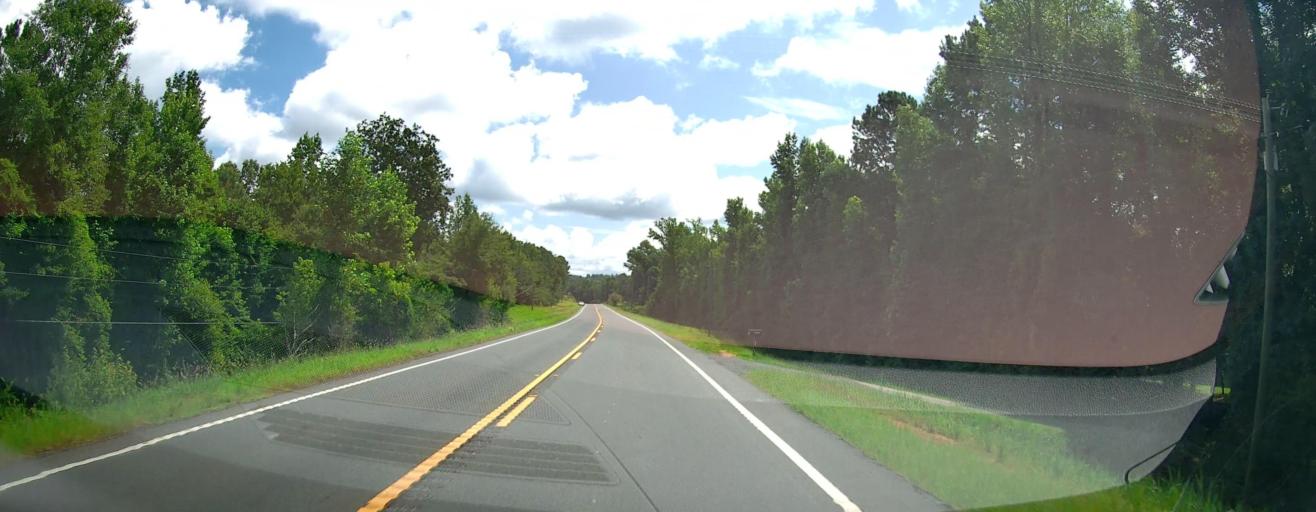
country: US
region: Georgia
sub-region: Bibb County
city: West Point
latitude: 32.7968
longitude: -83.8732
